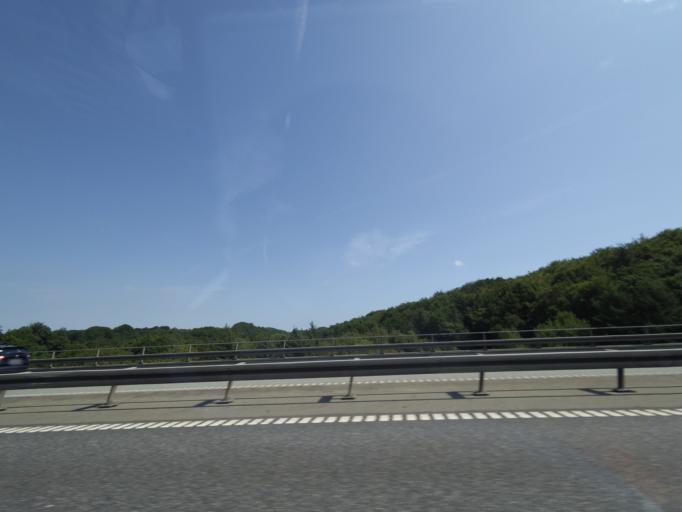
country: DK
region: South Denmark
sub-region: Fredericia Kommune
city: Taulov
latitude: 55.5678
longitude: 9.6167
